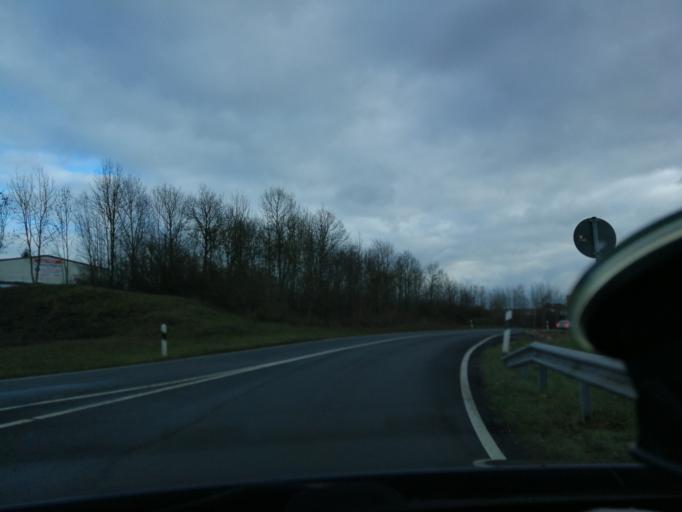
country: DE
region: Rheinland-Pfalz
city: Wittlich
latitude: 49.9790
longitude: 6.8972
